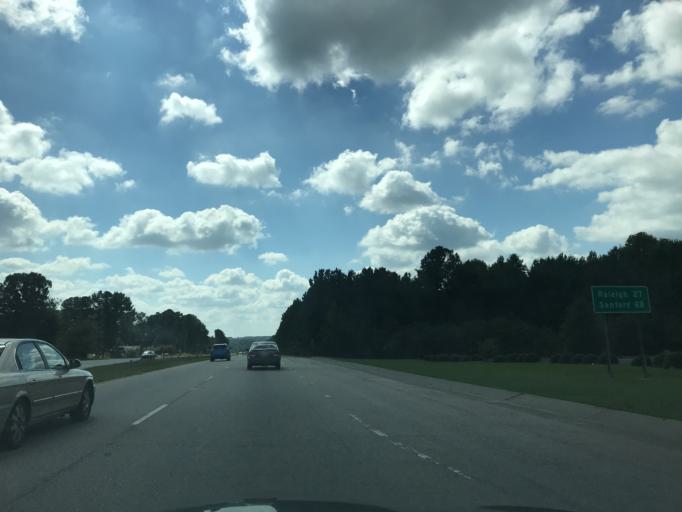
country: US
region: North Carolina
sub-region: Franklin County
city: Franklinton
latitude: 36.0969
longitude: -78.4691
